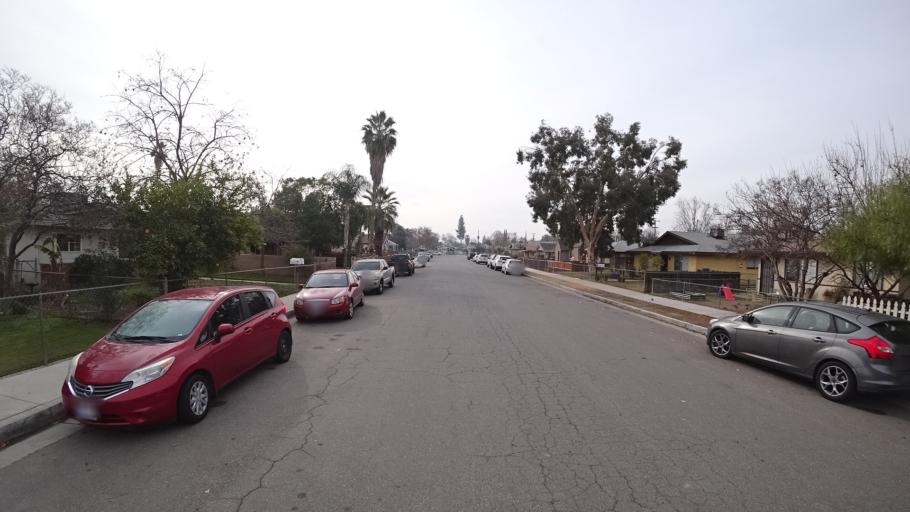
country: US
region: California
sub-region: Kern County
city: Bakersfield
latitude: 35.3610
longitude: -119.0244
